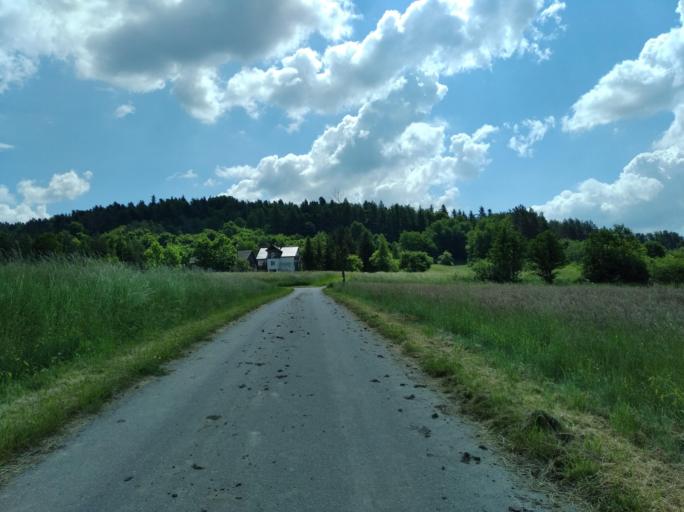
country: PL
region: Subcarpathian Voivodeship
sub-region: Powiat strzyzowski
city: Jawornik
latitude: 49.7831
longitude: 21.8683
